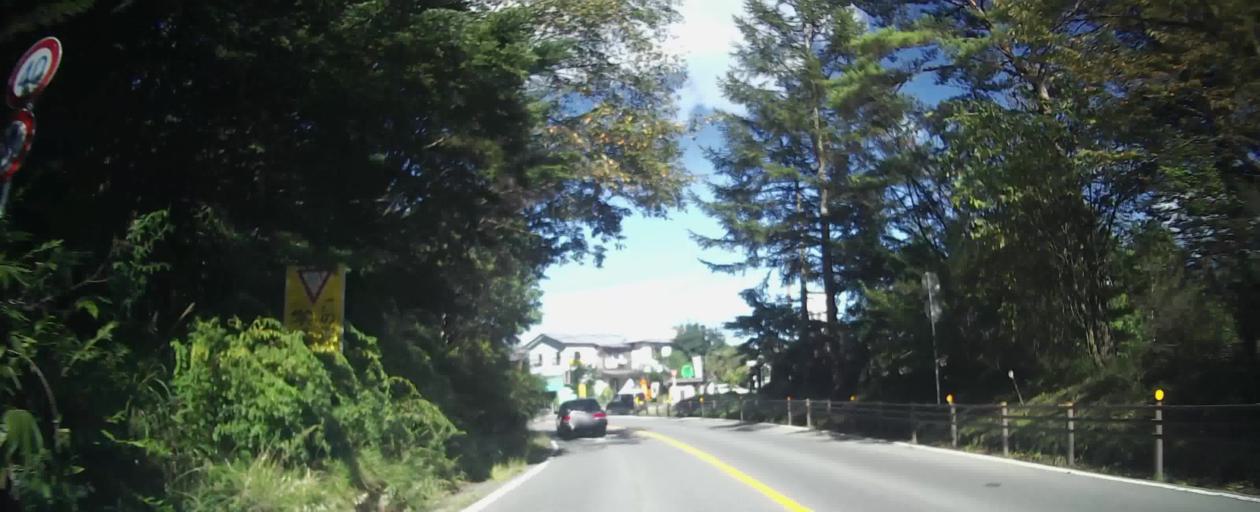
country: JP
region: Gunma
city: Nakanojomachi
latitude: 36.6160
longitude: 138.5918
